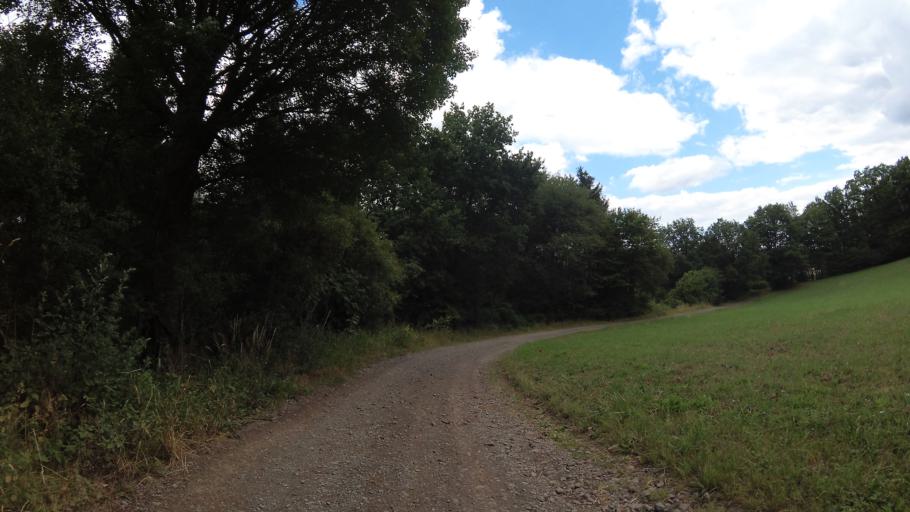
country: DE
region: Saarland
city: Sankt Wendel
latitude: 49.4975
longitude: 7.1880
